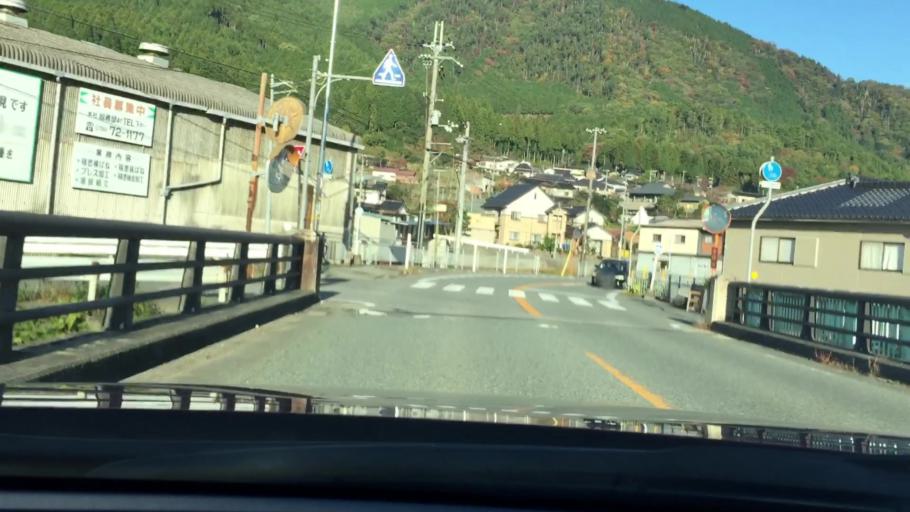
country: JP
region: Hyogo
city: Yamazakicho-nakabirose
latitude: 35.1173
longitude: 134.5689
